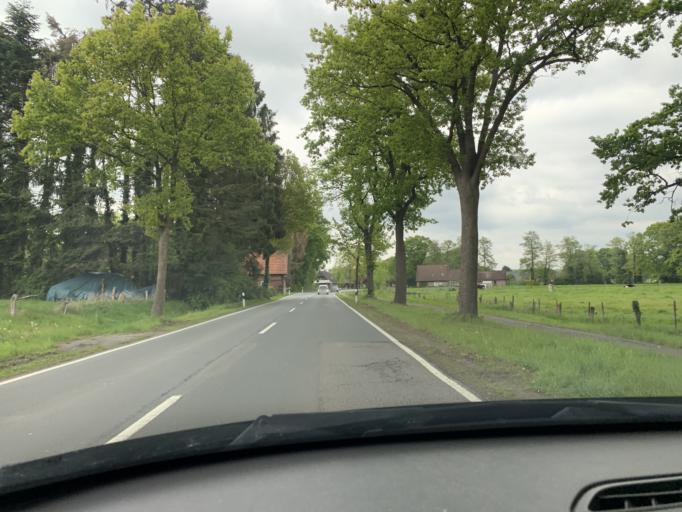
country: DE
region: Lower Saxony
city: Bad Zwischenahn
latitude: 53.2164
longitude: 8.0093
